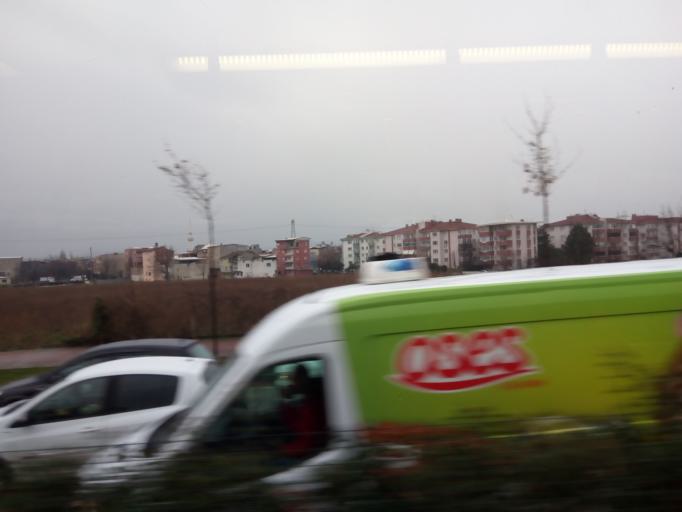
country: TR
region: Bursa
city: Yildirim
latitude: 40.2079
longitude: 29.0272
